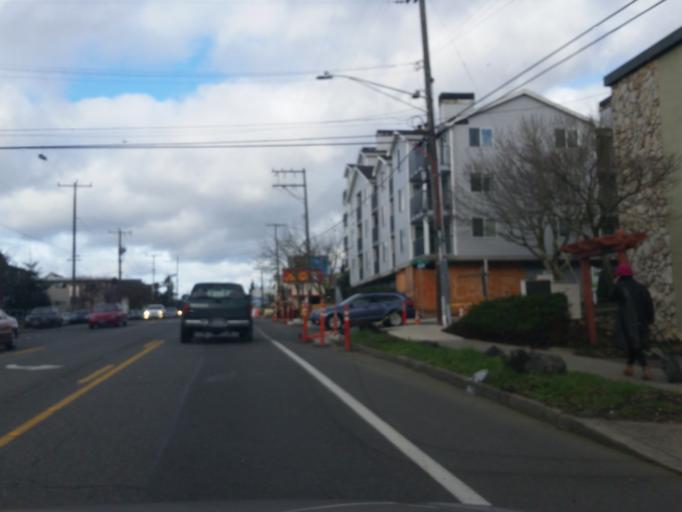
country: US
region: Washington
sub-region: King County
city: Shoreline
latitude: 47.6957
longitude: -122.3553
